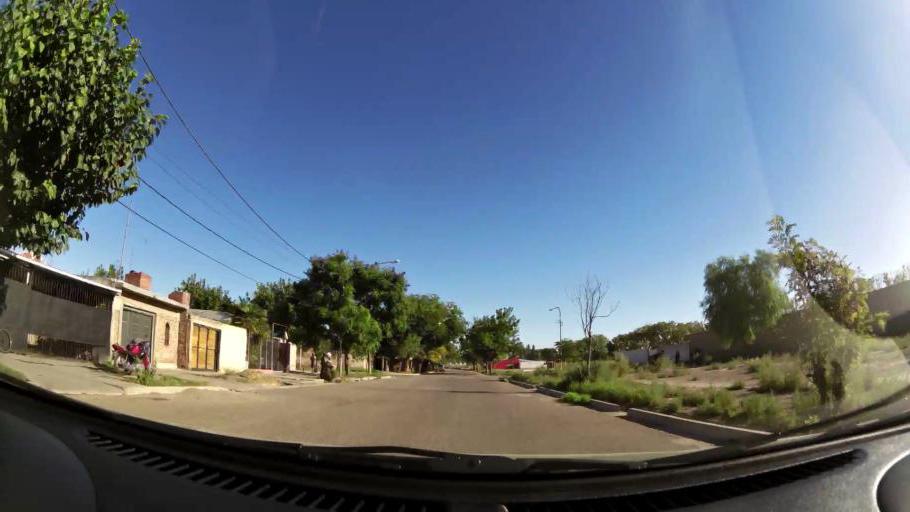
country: AR
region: Mendoza
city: Las Heras
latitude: -32.8453
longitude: -68.8256
